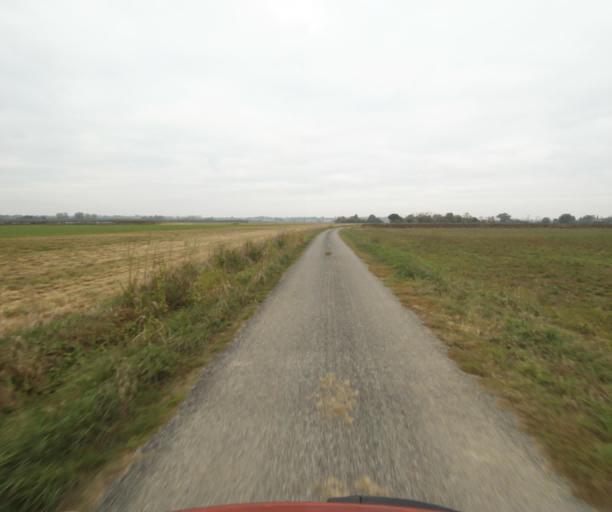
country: FR
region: Midi-Pyrenees
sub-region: Departement du Tarn-et-Garonne
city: Verdun-sur-Garonne
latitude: 43.8108
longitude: 1.2371
